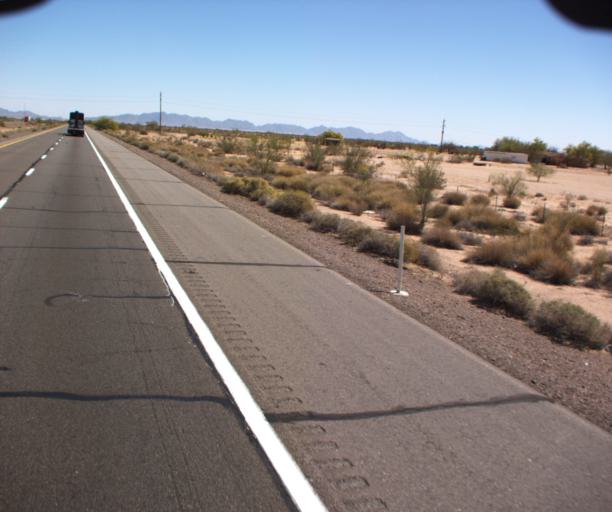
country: US
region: Arizona
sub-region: Yuma County
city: Wellton
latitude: 32.6877
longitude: -113.9902
